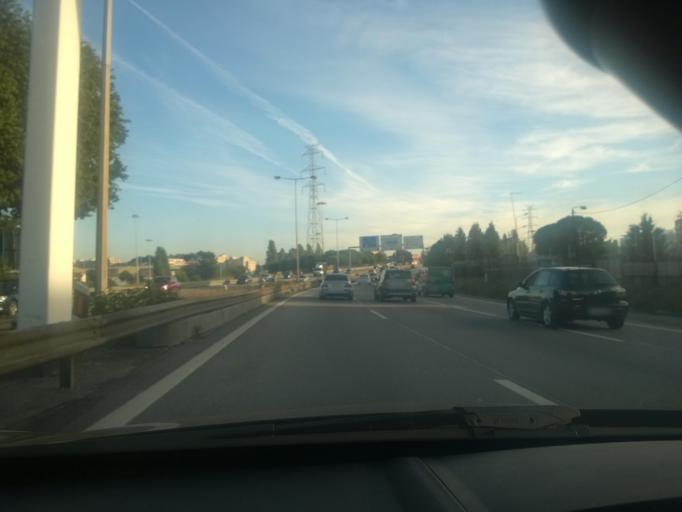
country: PT
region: Porto
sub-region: Matosinhos
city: Sao Mamede de Infesta
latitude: 41.1832
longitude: -8.6228
